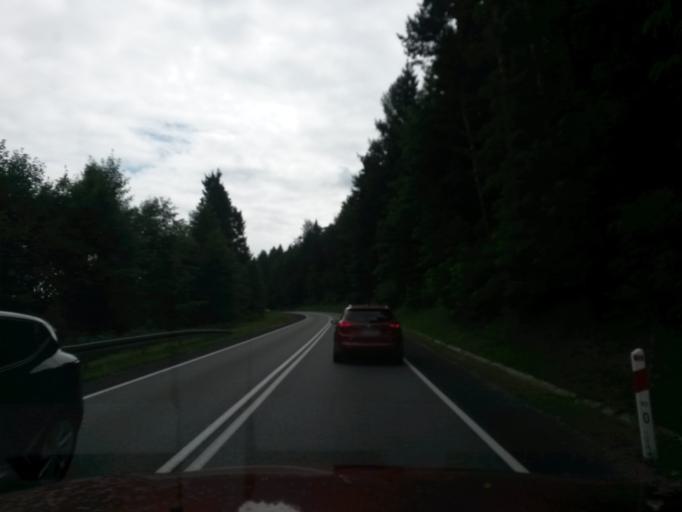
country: PL
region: Lesser Poland Voivodeship
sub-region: Powiat nowosadecki
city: Krynica-Zdroj
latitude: 49.4703
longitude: 20.9459
